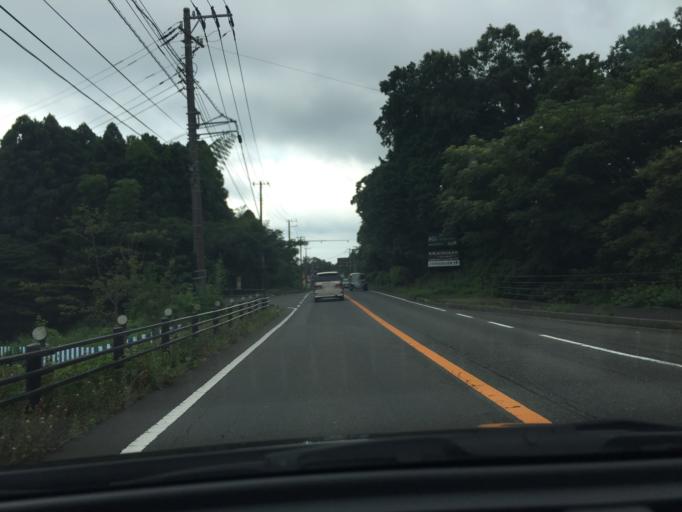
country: JP
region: Shizuoka
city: Ito
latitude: 34.9217
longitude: 139.1192
